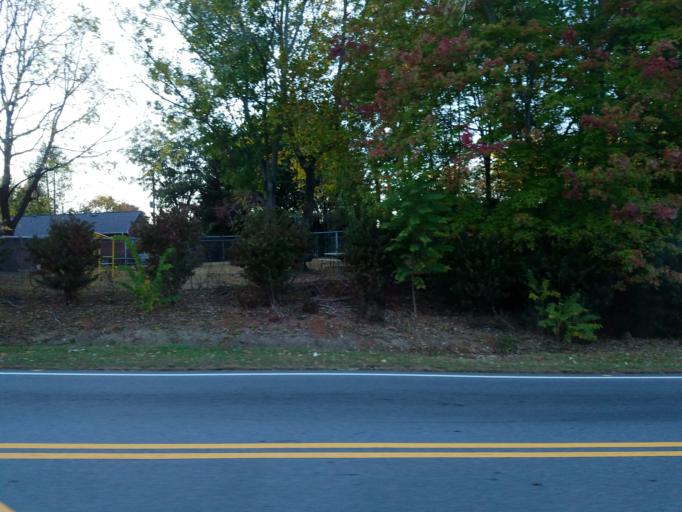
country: US
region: Georgia
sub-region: Lumpkin County
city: Dahlonega
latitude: 34.5258
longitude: -83.9799
